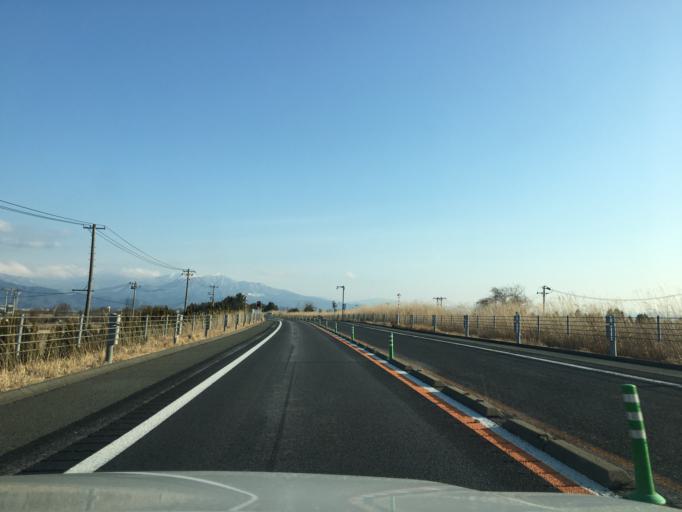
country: JP
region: Yamagata
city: Sagae
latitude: 38.3253
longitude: 140.2989
